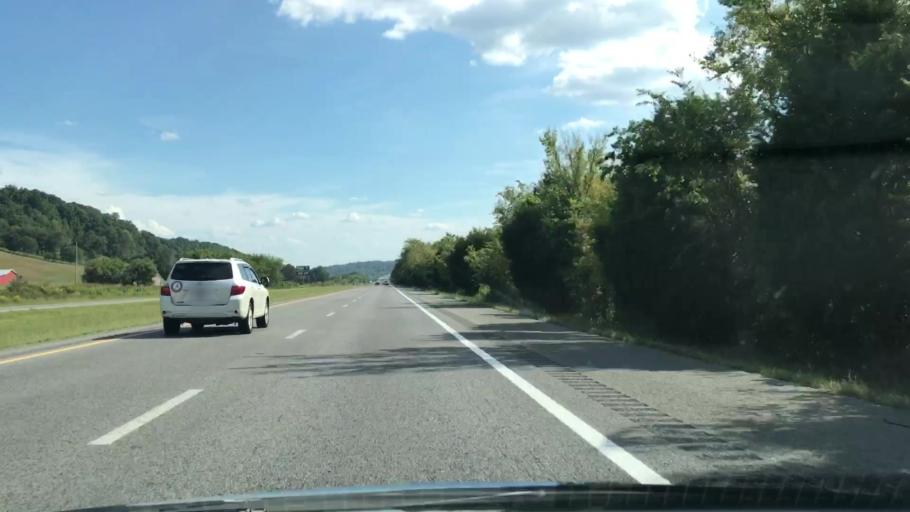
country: US
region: Tennessee
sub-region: Giles County
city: Pulaski
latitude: 35.1580
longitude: -86.8799
